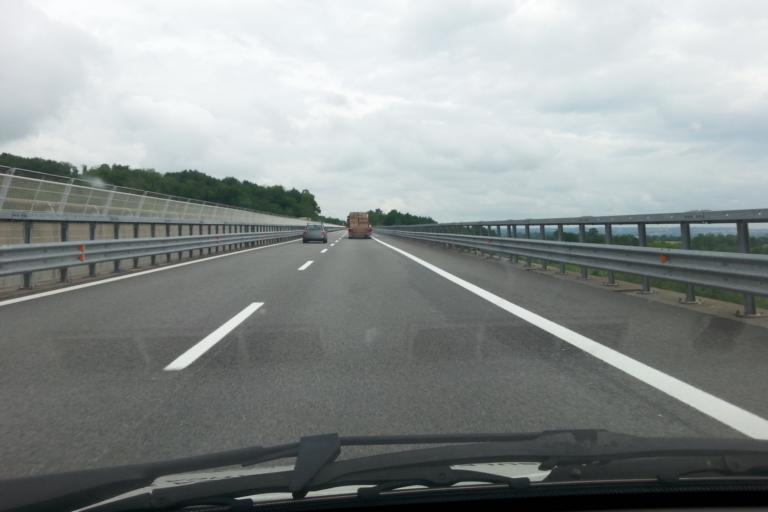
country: IT
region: Piedmont
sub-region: Provincia di Cuneo
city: Niella Tanaro
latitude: 44.4092
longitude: 7.9146
